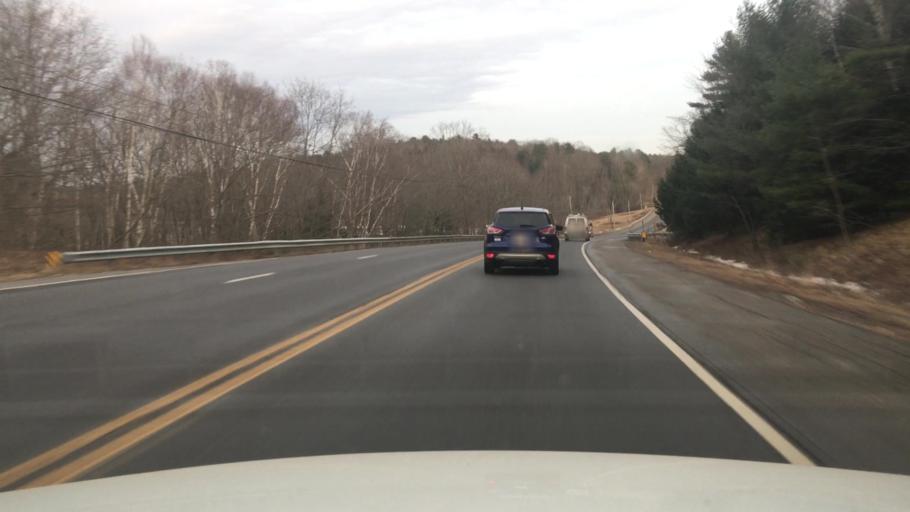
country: US
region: Maine
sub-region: Lincoln County
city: Edgecomb
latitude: 44.0108
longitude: -69.6009
